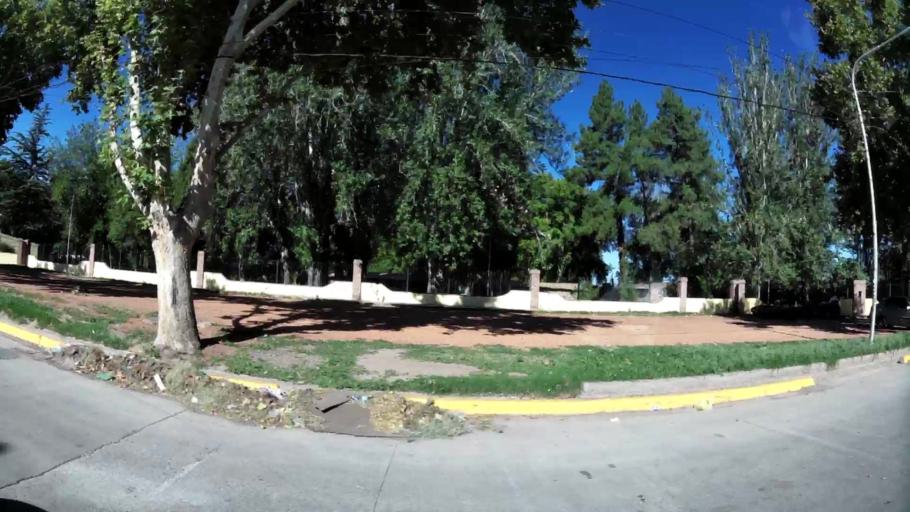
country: AR
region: Mendoza
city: Las Heras
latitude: -32.8437
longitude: -68.8198
